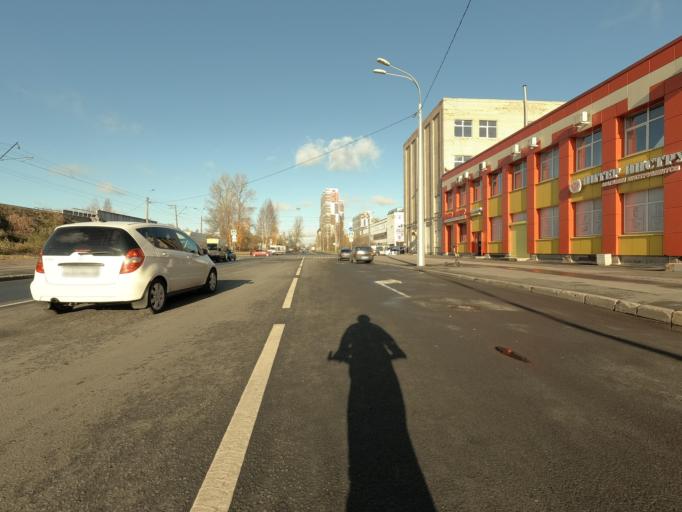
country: RU
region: St.-Petersburg
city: Krasnogvargeisky
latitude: 59.9523
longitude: 30.4476
